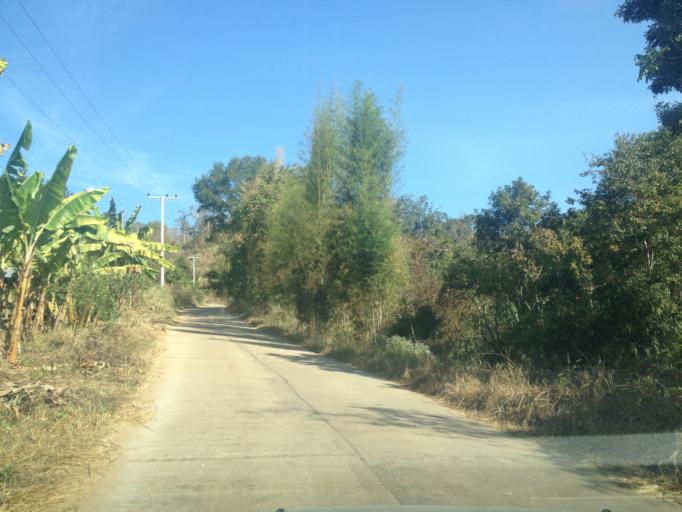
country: TH
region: Mae Hong Son
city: Ban Huai I Huak
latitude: 18.0634
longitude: 98.1835
